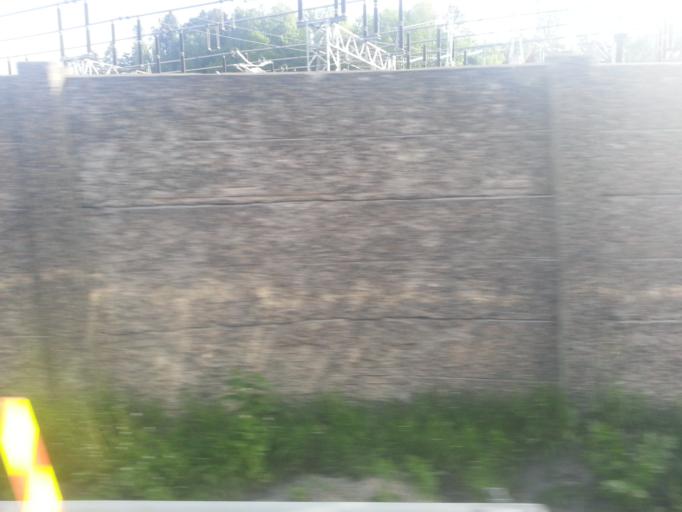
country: NO
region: Akershus
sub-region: Asker
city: Billingstad
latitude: 59.8972
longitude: 10.4998
